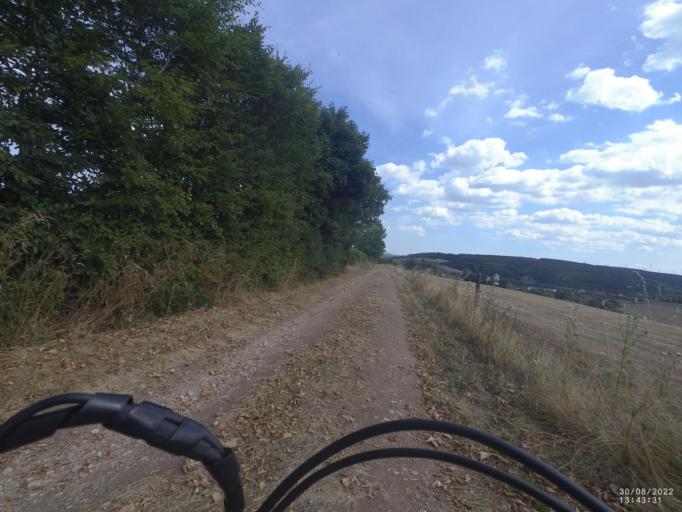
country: DE
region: Rheinland-Pfalz
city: Scheid
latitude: 50.3569
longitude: 6.4231
